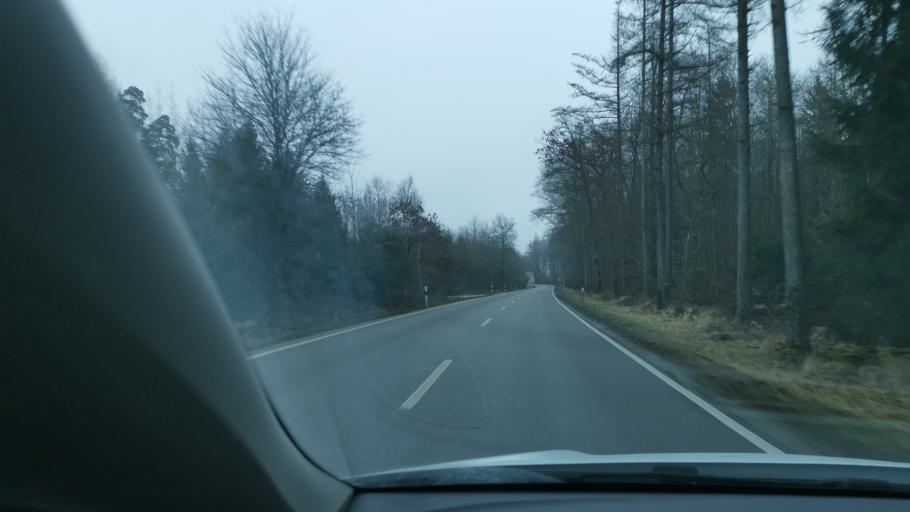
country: DE
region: Bavaria
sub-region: Swabia
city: Thierhaupten
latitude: 48.5858
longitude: 10.9302
